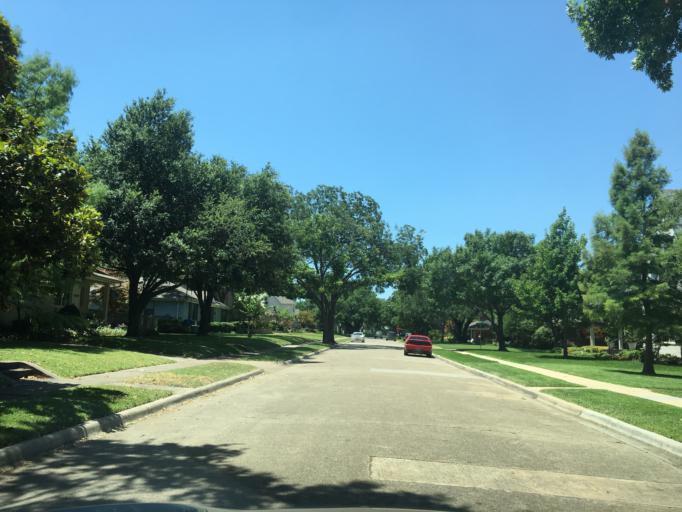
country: US
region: Texas
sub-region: Dallas County
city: Highland Park
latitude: 32.8344
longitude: -96.7415
